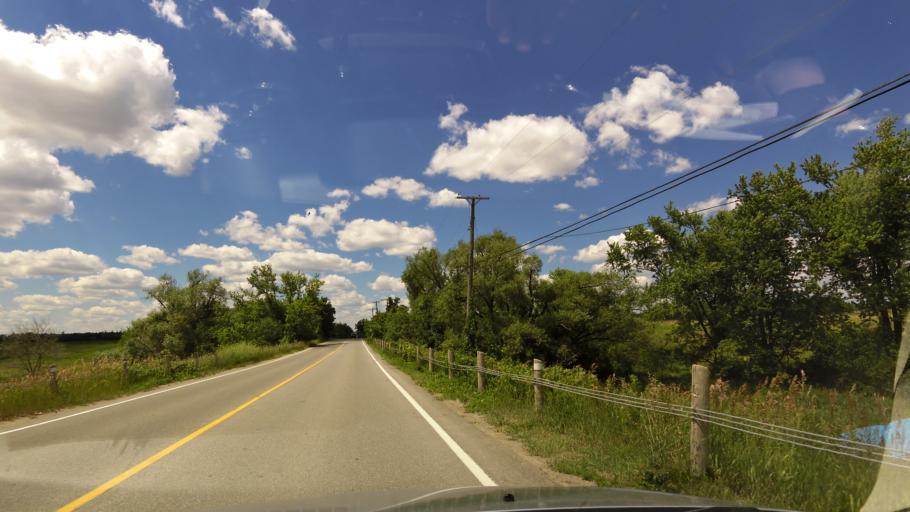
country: CA
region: Ontario
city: Brampton
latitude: 43.6222
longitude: -79.7925
